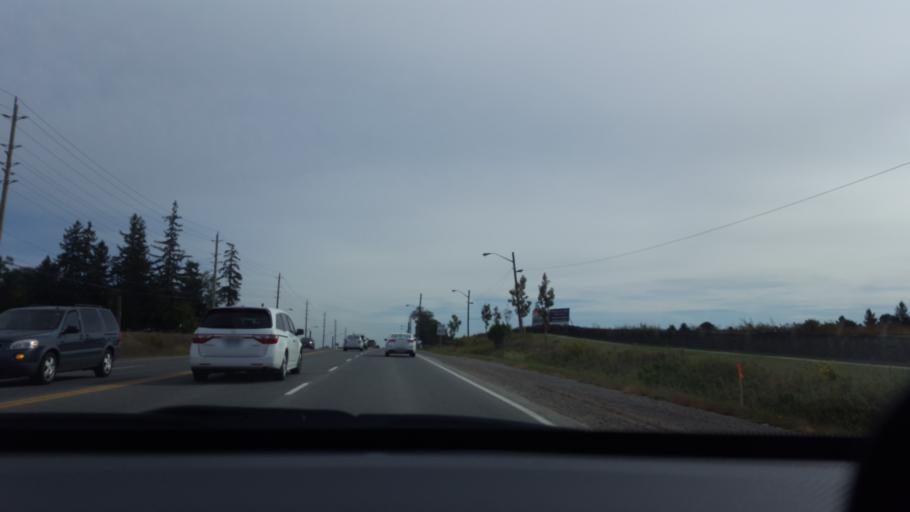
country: CA
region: Ontario
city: Newmarket
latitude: 44.0524
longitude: -79.4918
